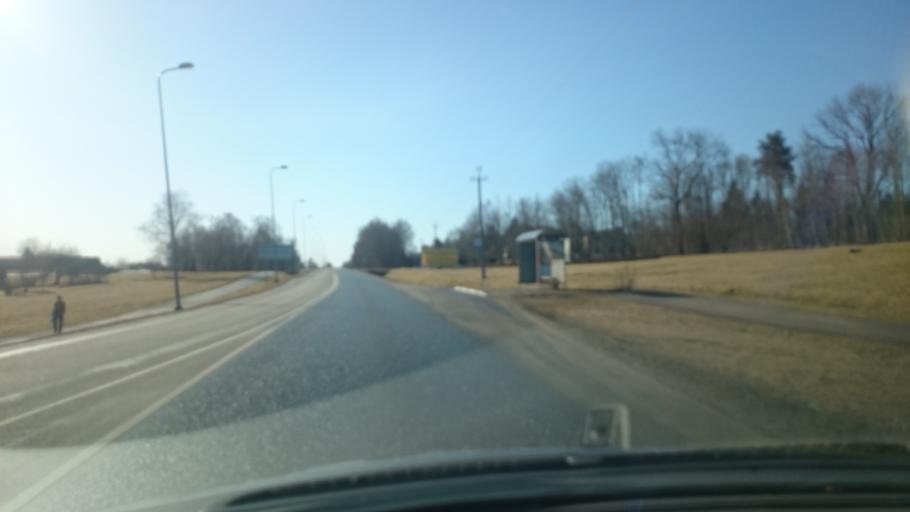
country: EE
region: Harju
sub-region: Saku vald
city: Saku
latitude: 59.3000
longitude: 24.6510
